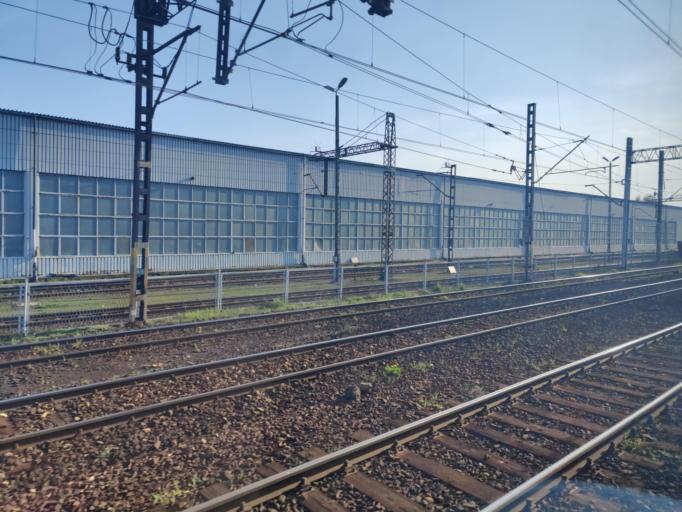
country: PL
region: Silesian Voivodeship
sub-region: Katowice
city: Katowice
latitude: 50.2574
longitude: 19.0437
